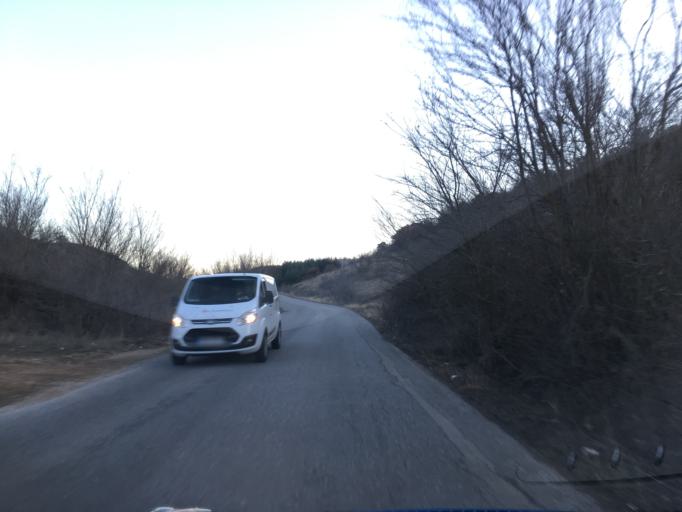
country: GR
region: West Macedonia
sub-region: Nomos Kozanis
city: Koila
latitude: 40.3280
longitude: 21.8121
